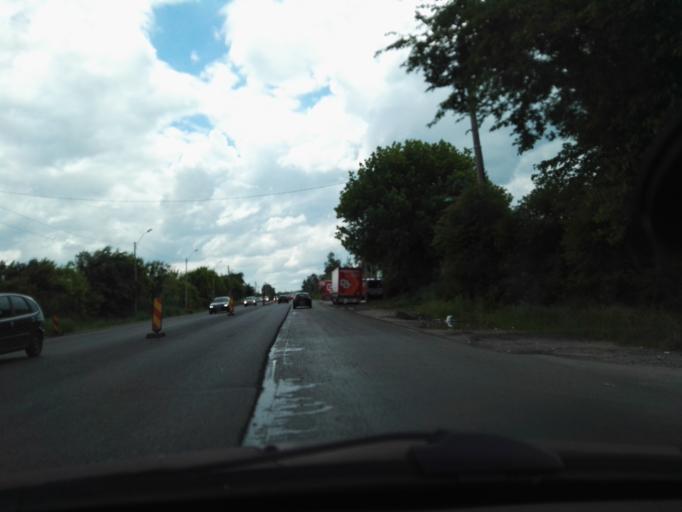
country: RO
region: Ilfov
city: Prim Decembrie
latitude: 44.2808
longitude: 26.0595
